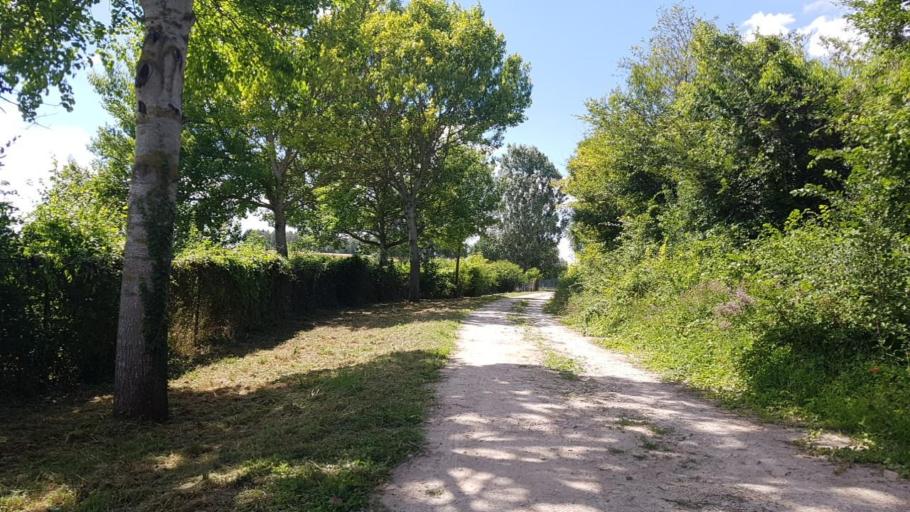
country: FR
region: Ile-de-France
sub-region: Departement de Seine-et-Marne
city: Moussy-le-Vieux
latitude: 49.0551
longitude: 2.6221
